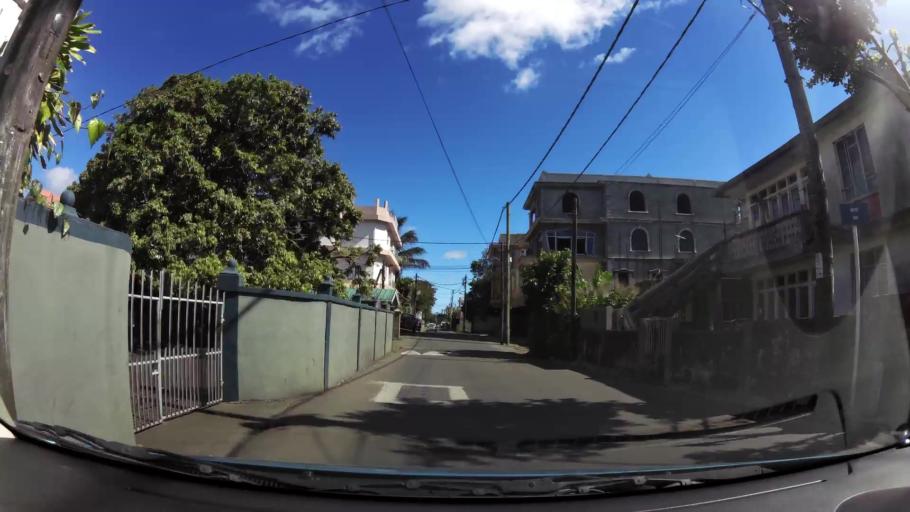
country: MU
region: Plaines Wilhems
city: Vacoas
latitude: -20.3135
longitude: 57.4833
